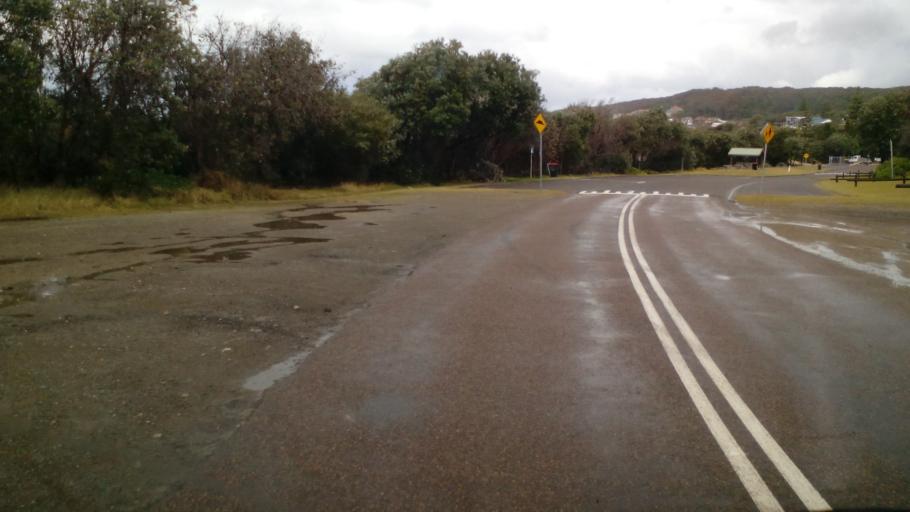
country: AU
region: New South Wales
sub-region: Lake Macquarie Shire
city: Belmont South
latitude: -33.1077
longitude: 151.6485
